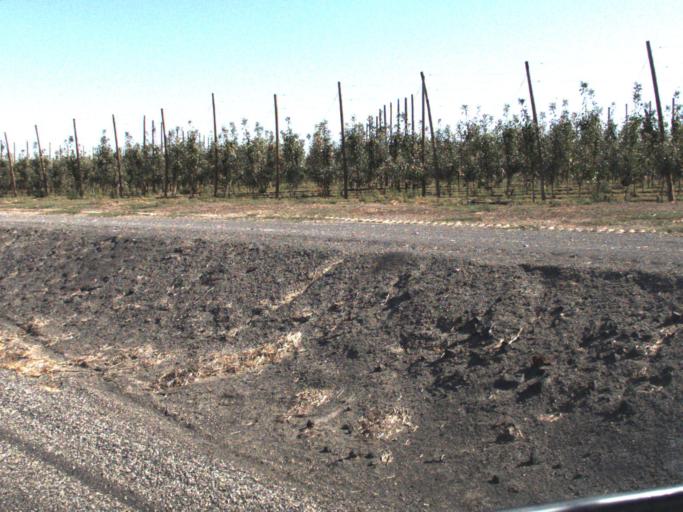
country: US
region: Washington
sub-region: Walla Walla County
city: Burbank
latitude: 46.2221
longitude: -118.8635
